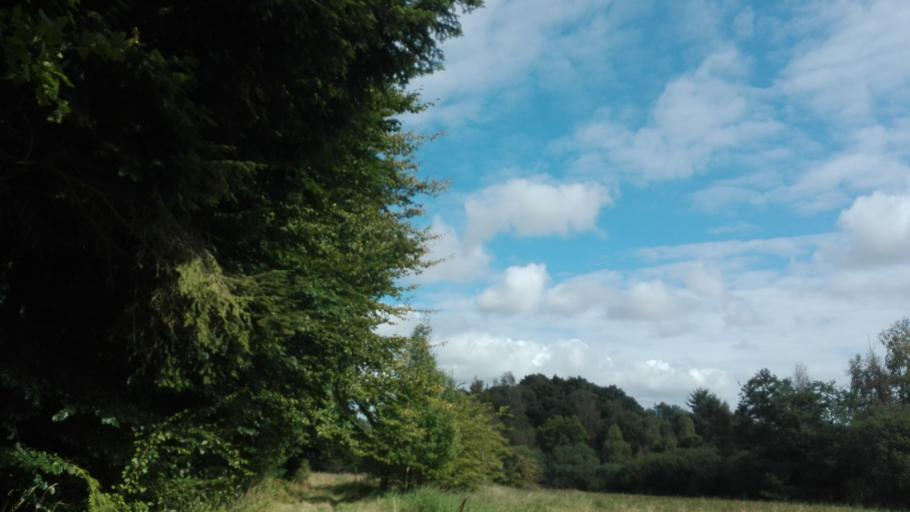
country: DK
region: Central Jutland
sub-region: Skanderborg Kommune
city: Stilling
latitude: 56.0947
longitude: 9.9808
